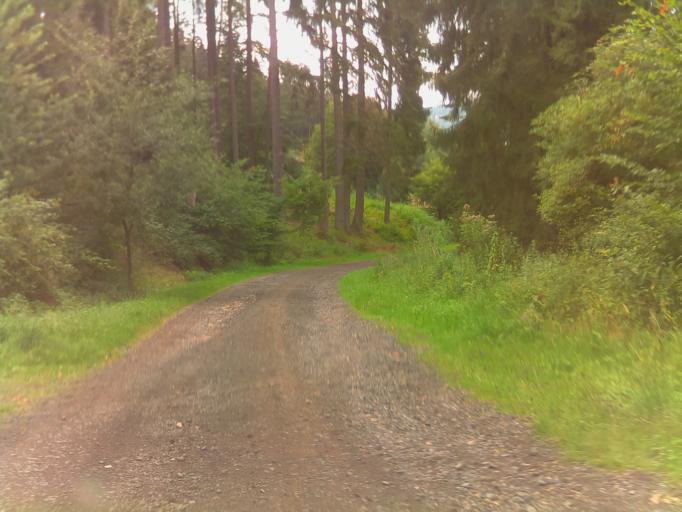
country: DE
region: Hesse
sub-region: Regierungsbezirk Darmstadt
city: Bad Orb
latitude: 50.2049
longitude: 9.3528
